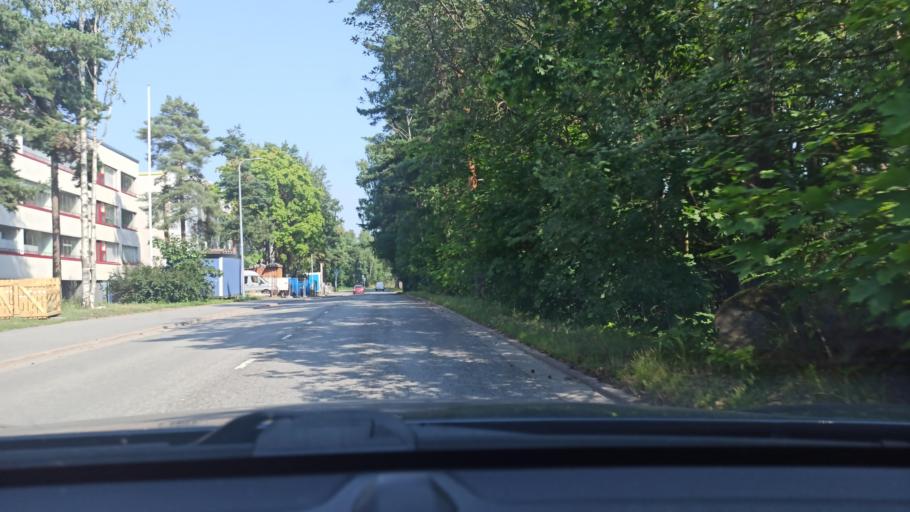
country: FI
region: Varsinais-Suomi
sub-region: Turku
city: Turku
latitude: 60.4612
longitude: 22.2218
